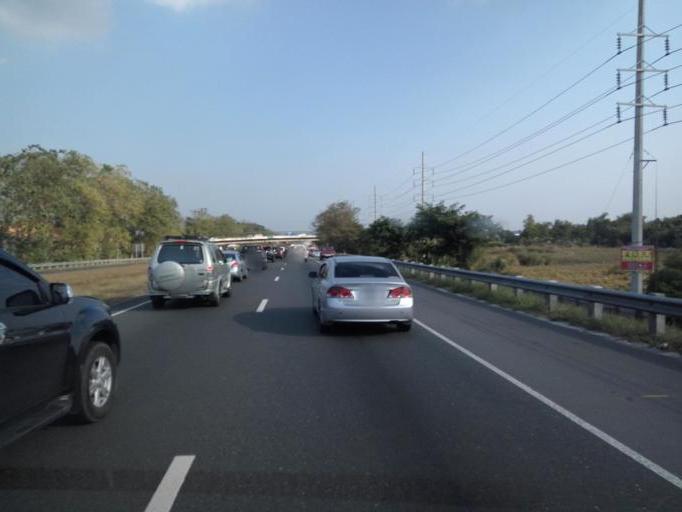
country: PH
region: Central Luzon
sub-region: Province of Pampanga
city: Acli
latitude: 15.1101
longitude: 120.6602
